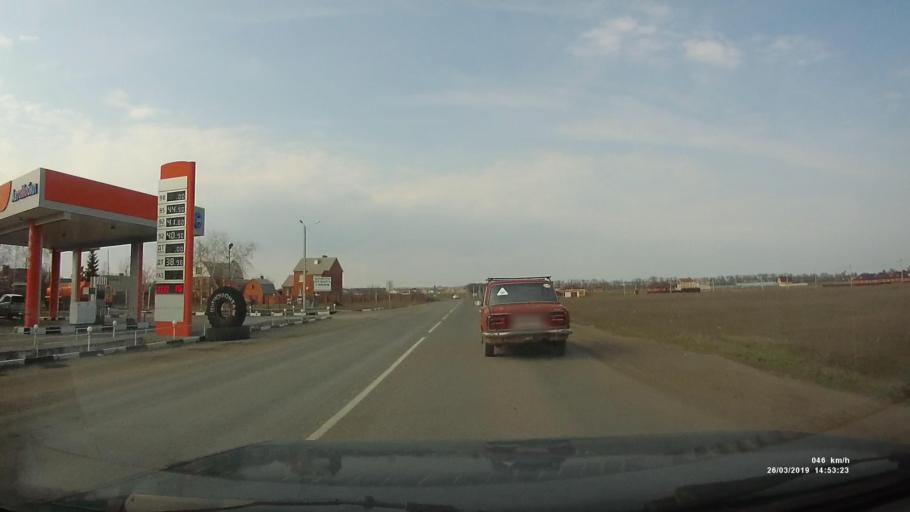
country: RU
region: Rostov
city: Novobessergenovka
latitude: 47.1847
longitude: 38.8141
